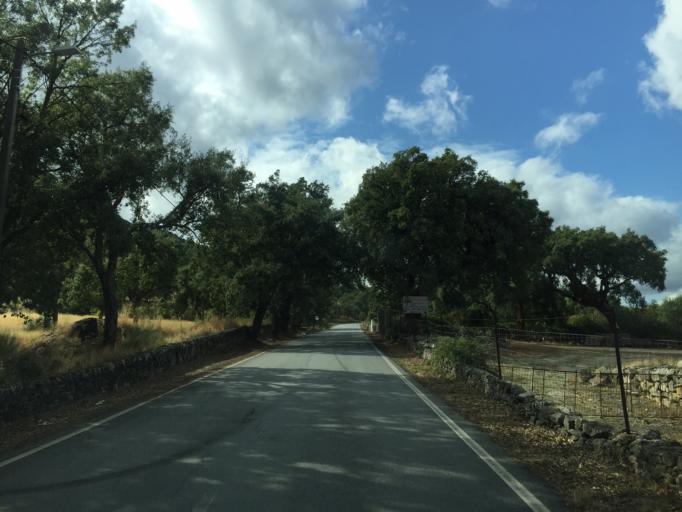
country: PT
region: Portalegre
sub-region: Marvao
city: Marvao
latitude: 39.4003
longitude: -7.3721
